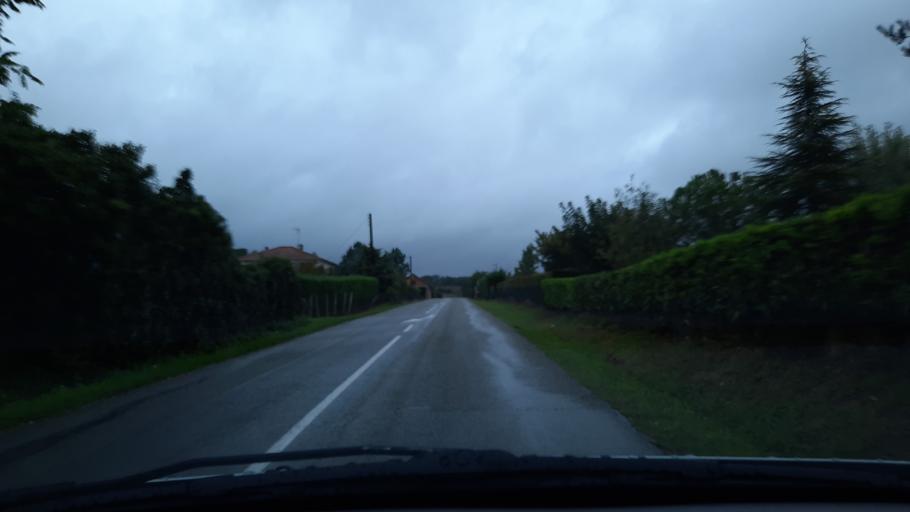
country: FR
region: Midi-Pyrenees
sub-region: Departement du Tarn-et-Garonne
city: Lafrancaise
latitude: 44.1919
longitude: 1.2850
